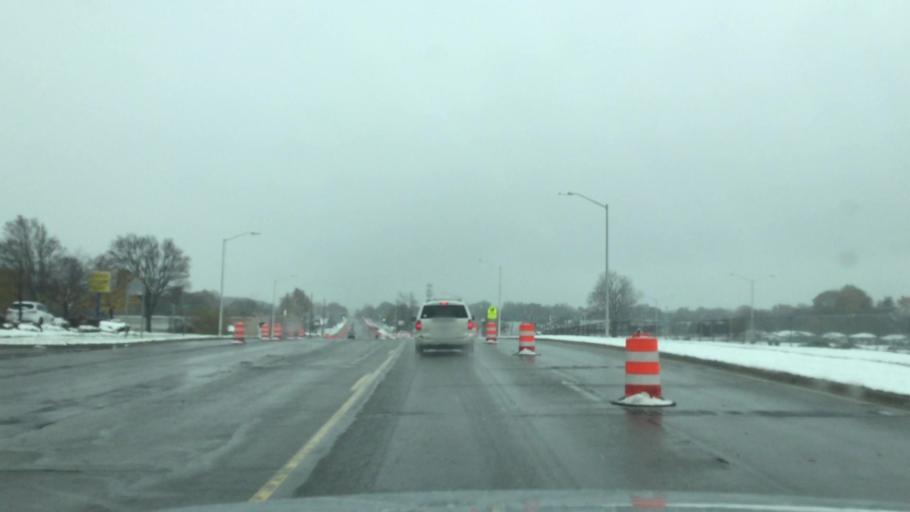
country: US
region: Michigan
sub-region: Oakland County
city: Pontiac
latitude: 42.6652
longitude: -83.2656
